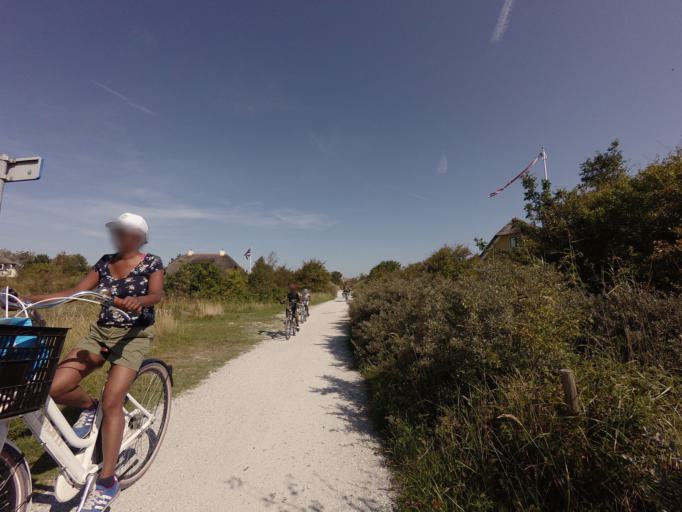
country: NL
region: Friesland
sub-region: Gemeente Schiermonnikoog
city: Schiermonnikoog
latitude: 53.4863
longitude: 6.1497
